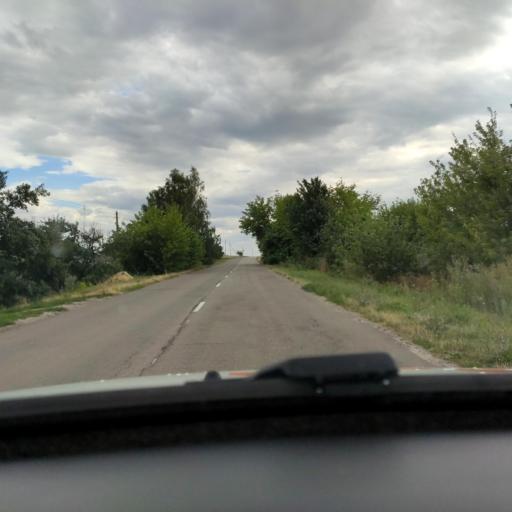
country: RU
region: Voronezj
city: Orlovo
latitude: 51.6803
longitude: 39.5740
